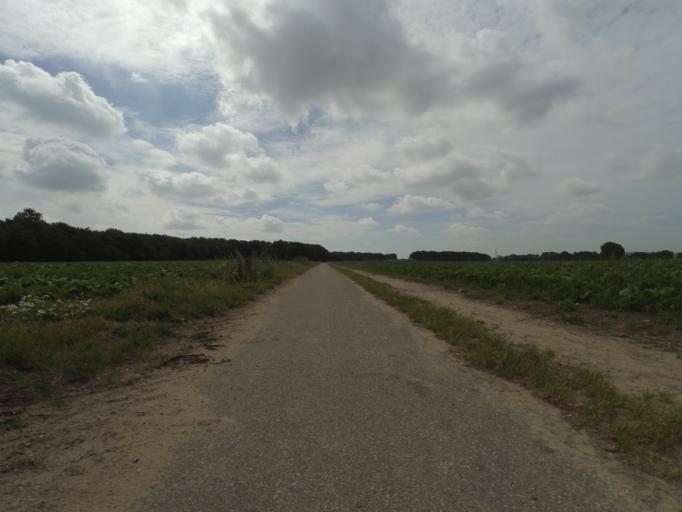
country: NL
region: Utrecht
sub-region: Gemeente Rhenen
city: Rhenen
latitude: 51.9738
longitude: 5.5446
